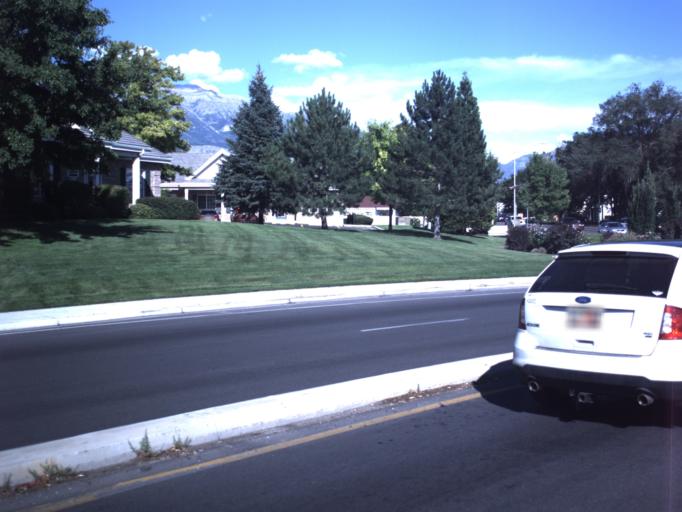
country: US
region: Utah
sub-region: Utah County
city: American Fork
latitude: 40.3773
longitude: -111.8120
